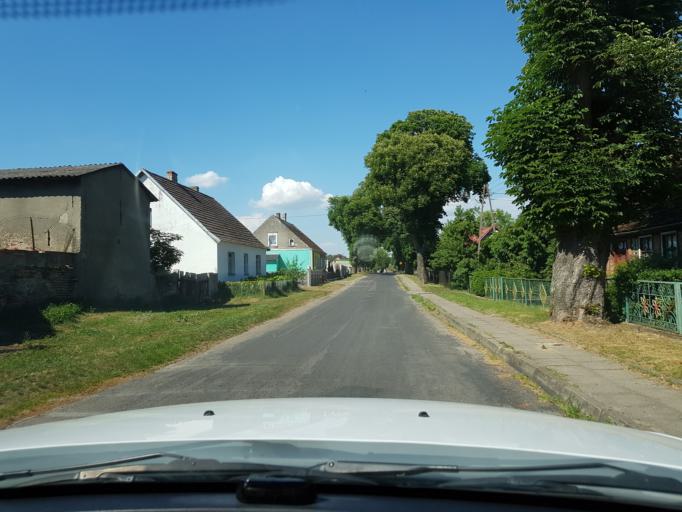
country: PL
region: West Pomeranian Voivodeship
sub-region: Powiat gryfinski
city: Gryfino
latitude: 53.1705
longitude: 14.5407
